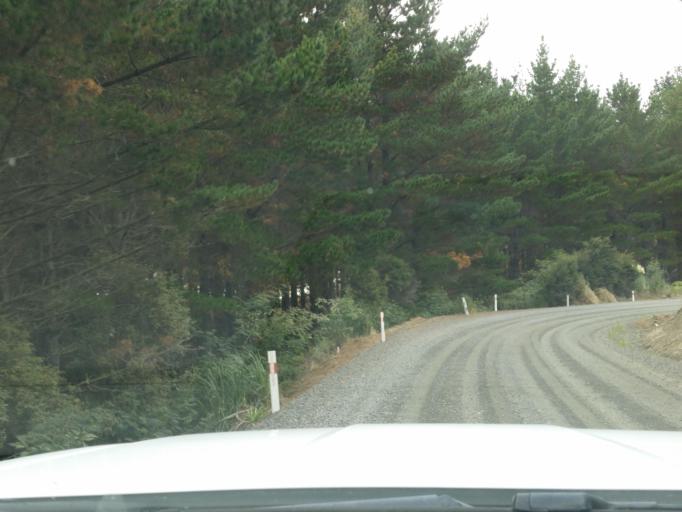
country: NZ
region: Northland
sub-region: Kaipara District
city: Dargaville
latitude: -36.2436
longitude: 174.0932
